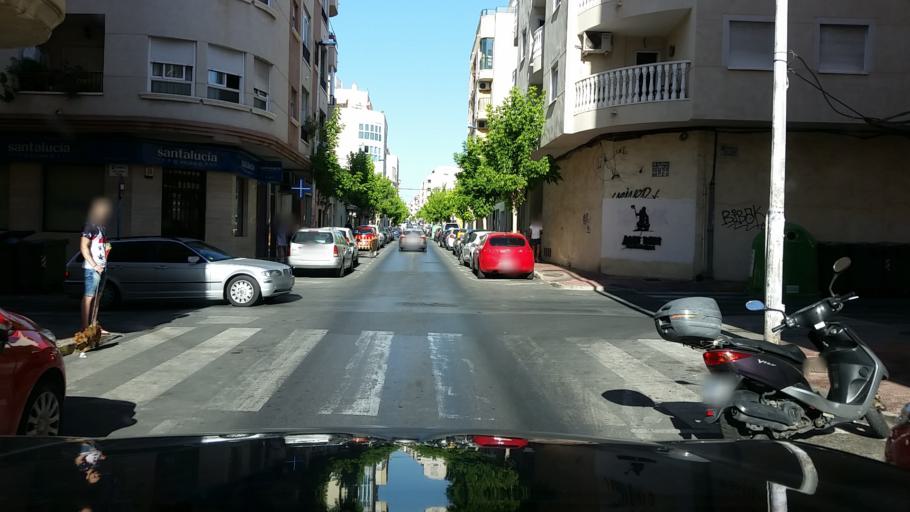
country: ES
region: Valencia
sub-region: Provincia de Alicante
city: Torrevieja
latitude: 37.9812
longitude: -0.6799
